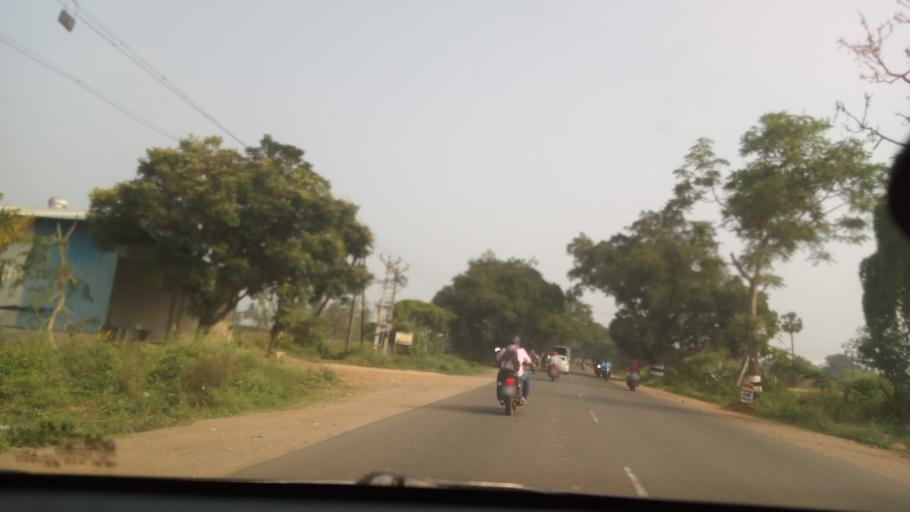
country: IN
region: Tamil Nadu
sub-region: Coimbatore
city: Annur
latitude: 11.1582
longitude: 77.0505
